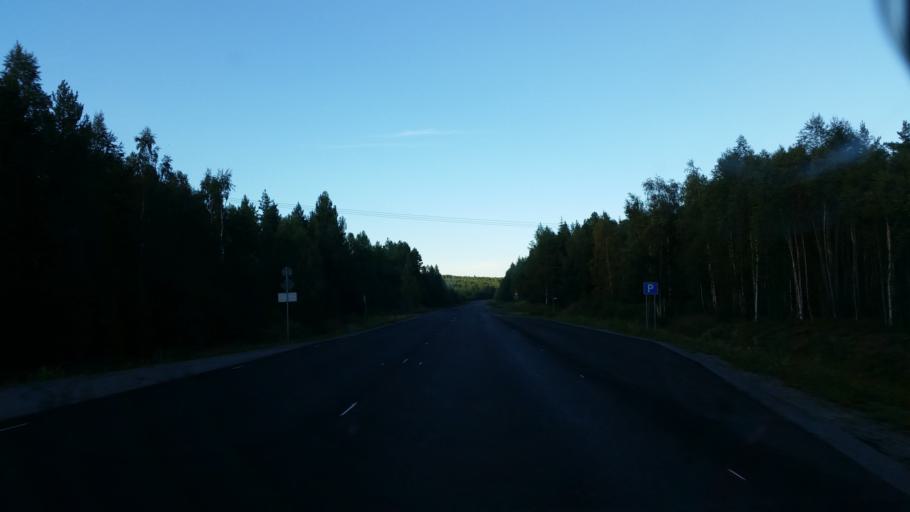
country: SE
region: Vaesterbotten
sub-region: Dorotea Kommun
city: Dorotea
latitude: 64.2949
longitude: 16.5408
